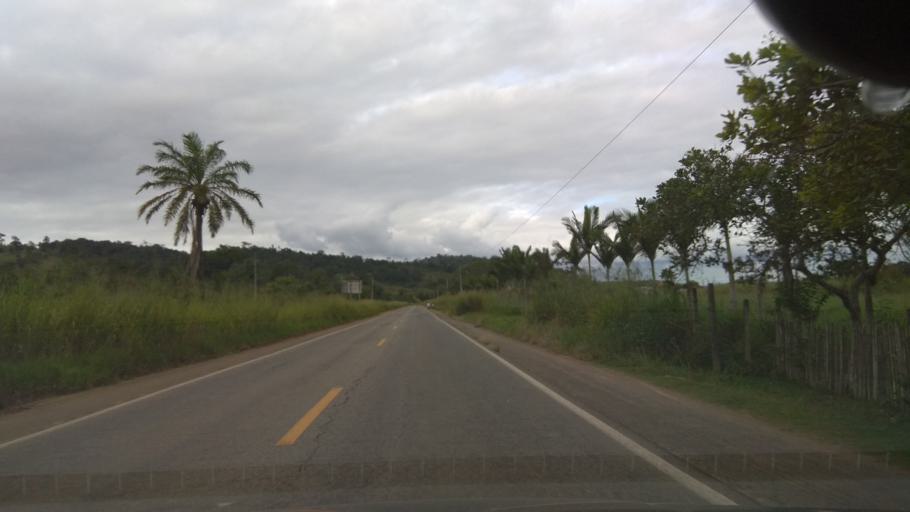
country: BR
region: Bahia
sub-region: Ipiau
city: Ipiau
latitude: -14.1461
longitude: -39.7091
